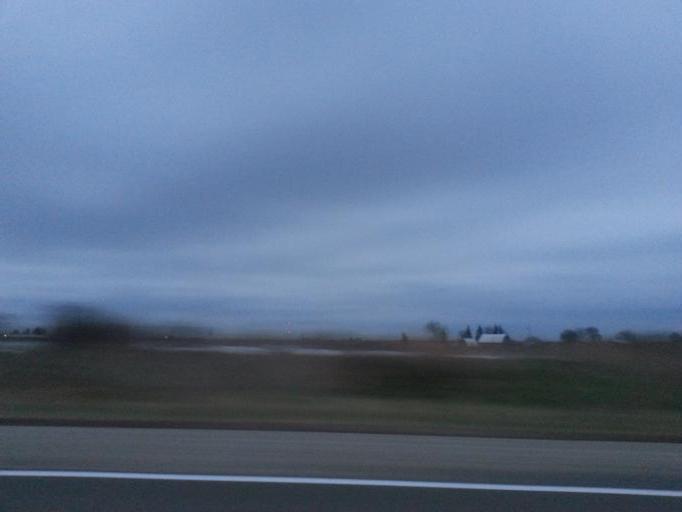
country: US
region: Iowa
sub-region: Black Hawk County
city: La Porte City
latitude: 42.3964
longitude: -92.1446
